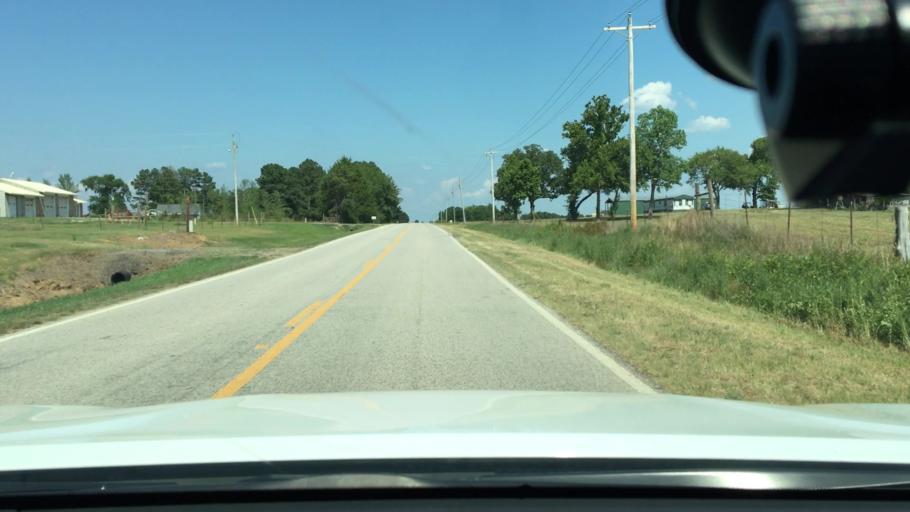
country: US
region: Arkansas
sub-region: Johnson County
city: Coal Hill
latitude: 35.3511
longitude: -93.5832
